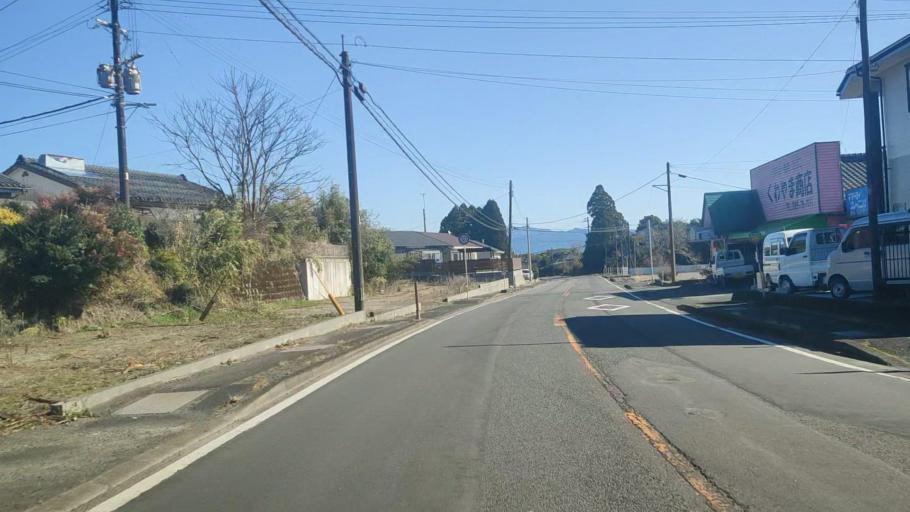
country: JP
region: Kagoshima
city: Sueyoshicho-ninokata
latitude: 31.6957
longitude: 130.9925
